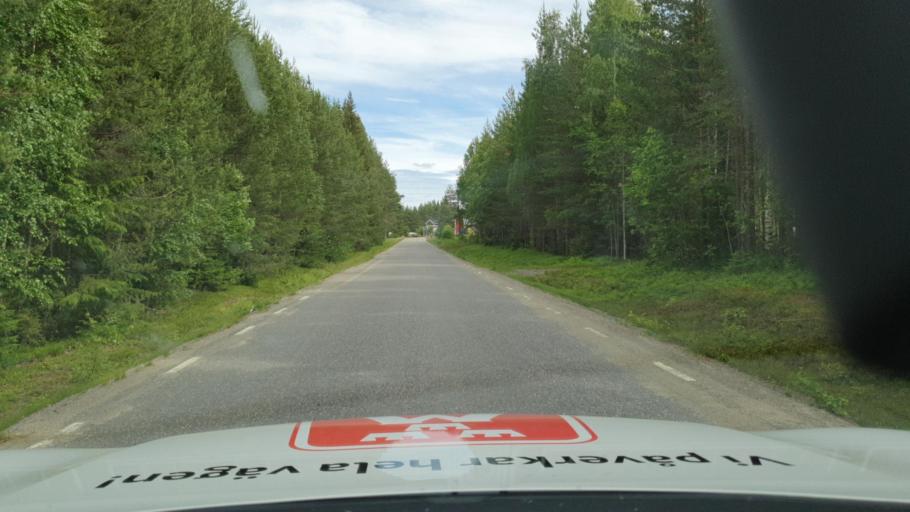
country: SE
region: Vaesterbotten
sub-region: Skelleftea Kommun
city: Viken
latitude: 64.4974
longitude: 20.9001
